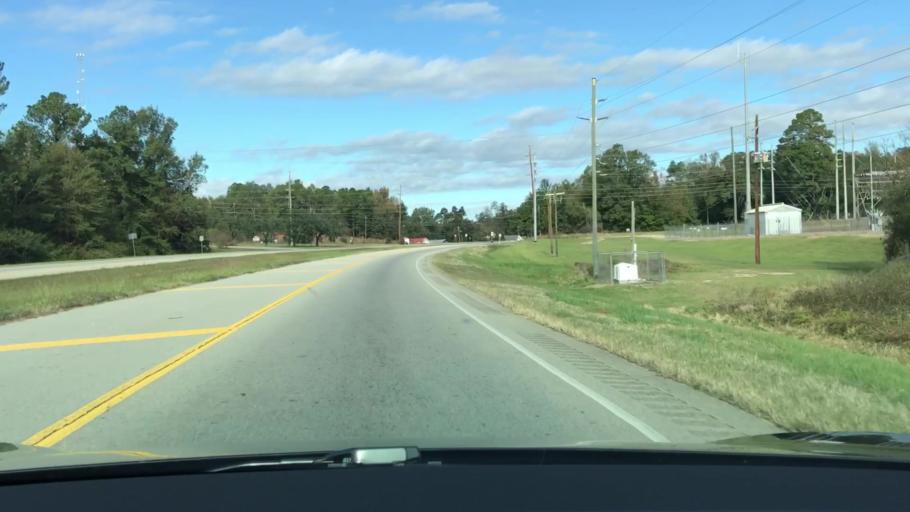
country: US
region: Georgia
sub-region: Jefferson County
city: Louisville
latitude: 33.0138
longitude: -82.4020
